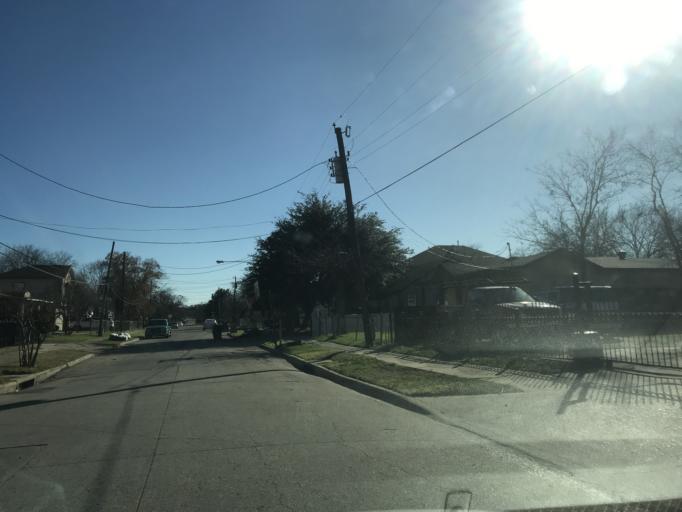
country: US
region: Texas
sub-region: Dallas County
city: Cockrell Hill
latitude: 32.7757
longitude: -96.9084
